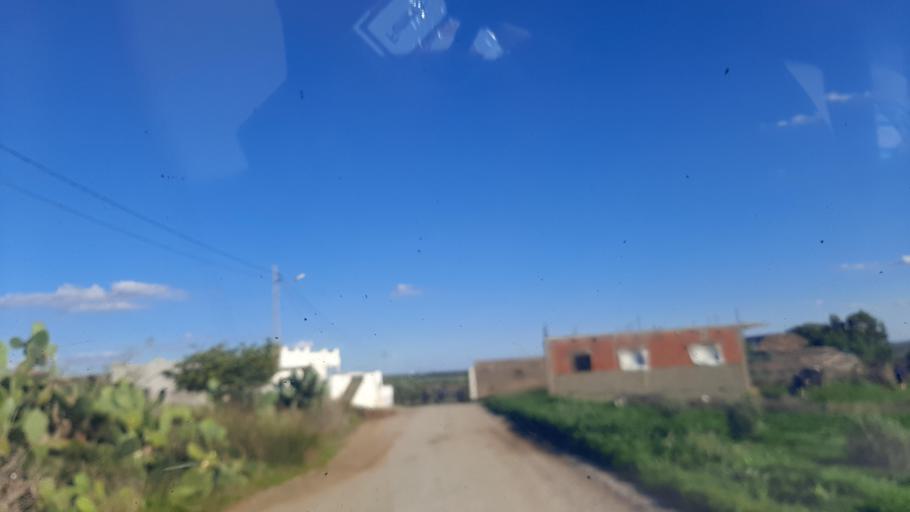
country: TN
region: Nabul
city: El Mida
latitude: 36.8380
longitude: 10.8298
